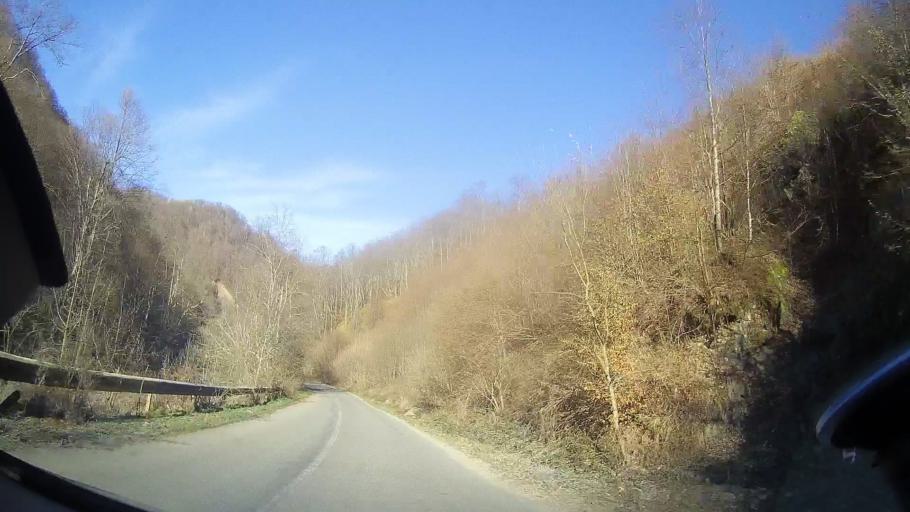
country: RO
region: Cluj
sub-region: Comuna Sacueu
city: Sacuieu
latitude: 46.8405
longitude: 22.8629
